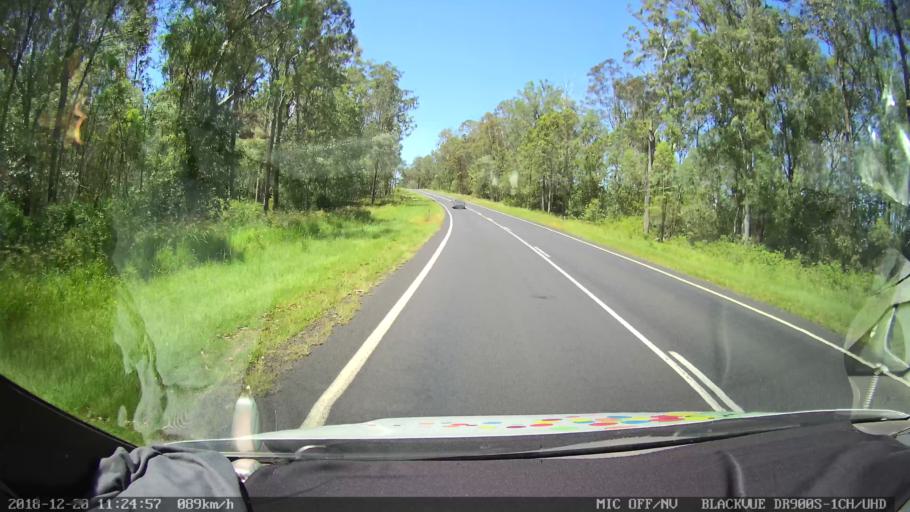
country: AU
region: New South Wales
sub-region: Richmond Valley
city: Casino
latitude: -29.0813
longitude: 153.0004
